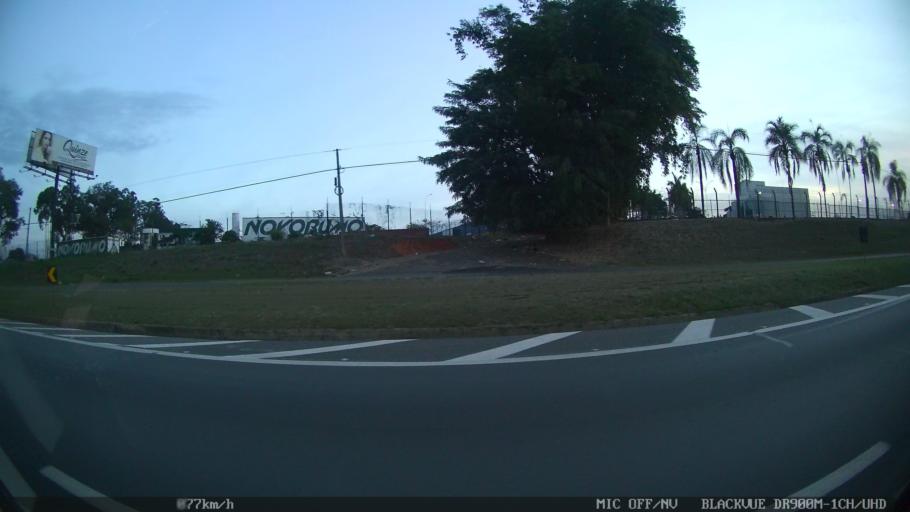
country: BR
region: Sao Paulo
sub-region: Limeira
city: Limeira
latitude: -22.6094
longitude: -47.3608
